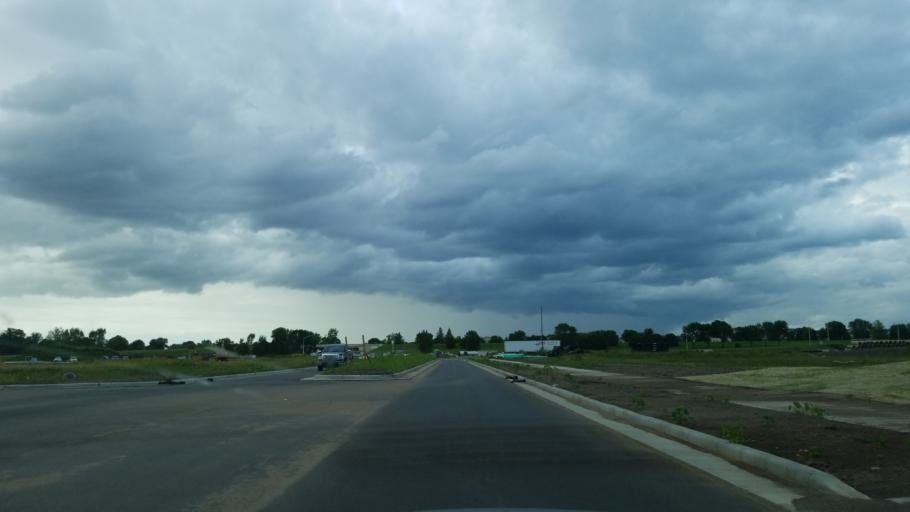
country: US
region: Minnesota
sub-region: Washington County
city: Lakeland
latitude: 44.9459
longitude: -92.7266
